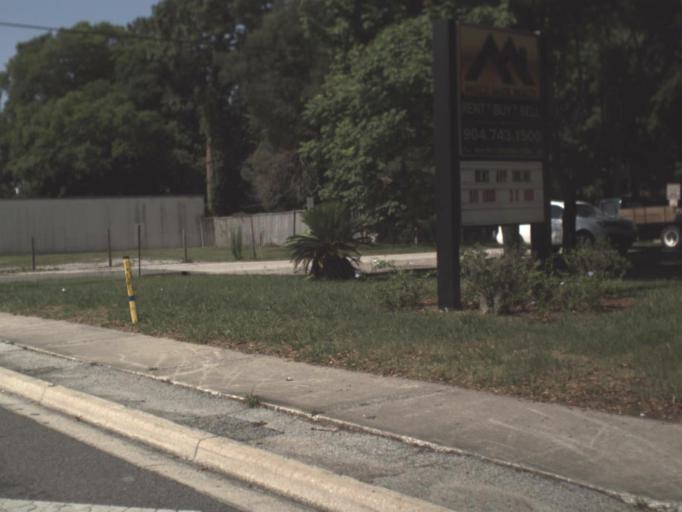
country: US
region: Florida
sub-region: Duval County
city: Jacksonville
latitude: 30.3389
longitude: -81.6026
